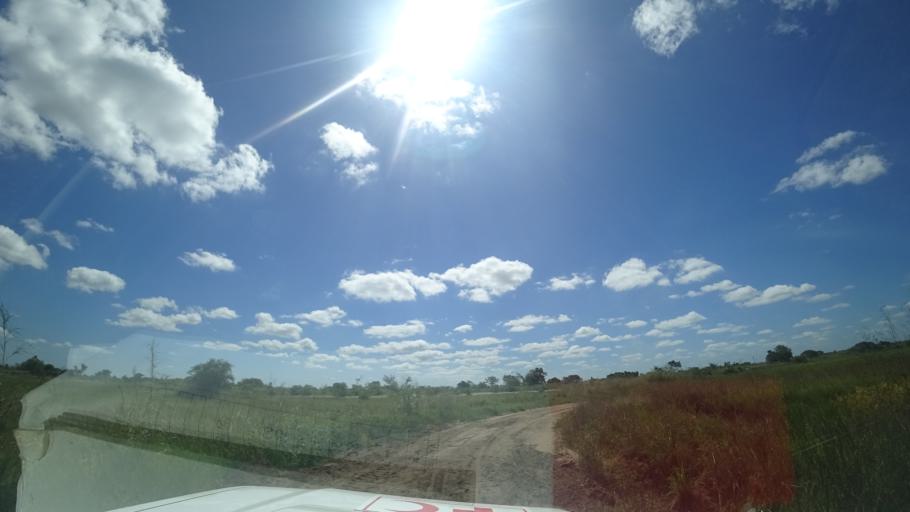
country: MZ
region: Sofala
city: Dondo
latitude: -19.4573
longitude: 34.5939
